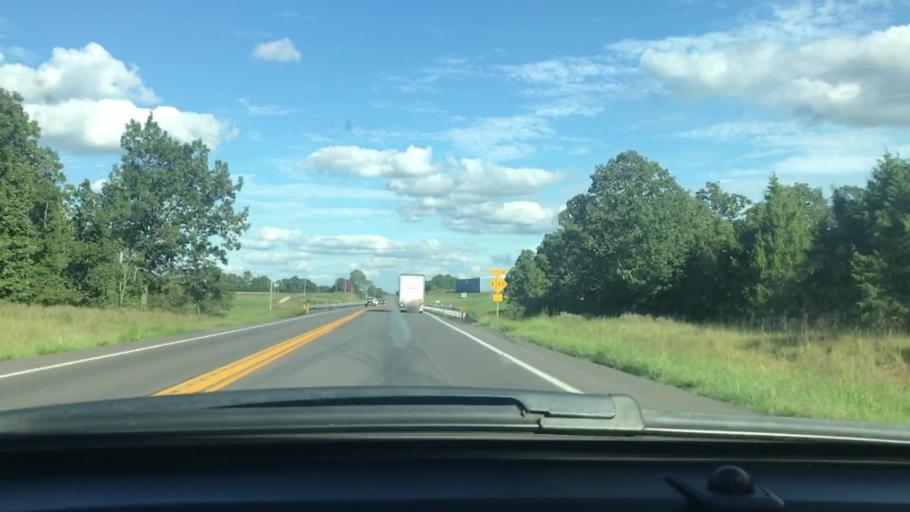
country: US
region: Missouri
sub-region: Oregon County
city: Thayer
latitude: 36.5886
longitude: -91.6372
